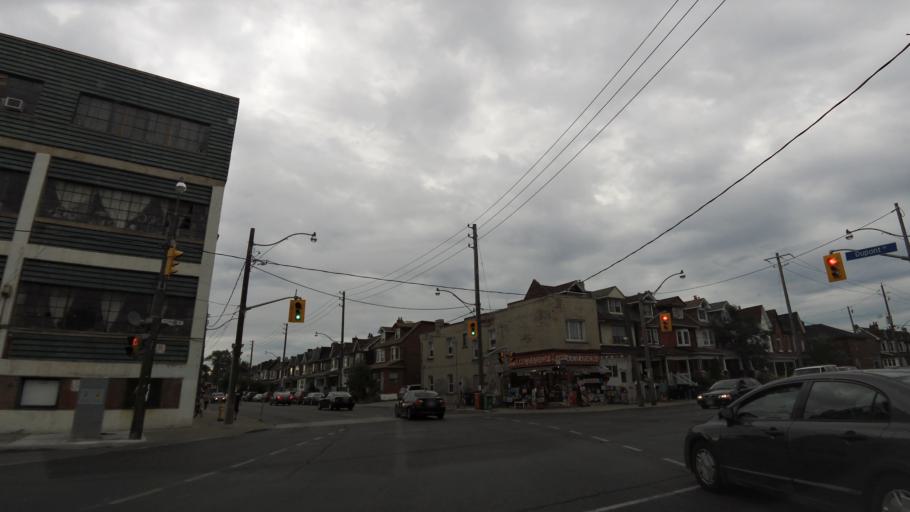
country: CA
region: Ontario
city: Toronto
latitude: 43.6702
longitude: -79.4292
